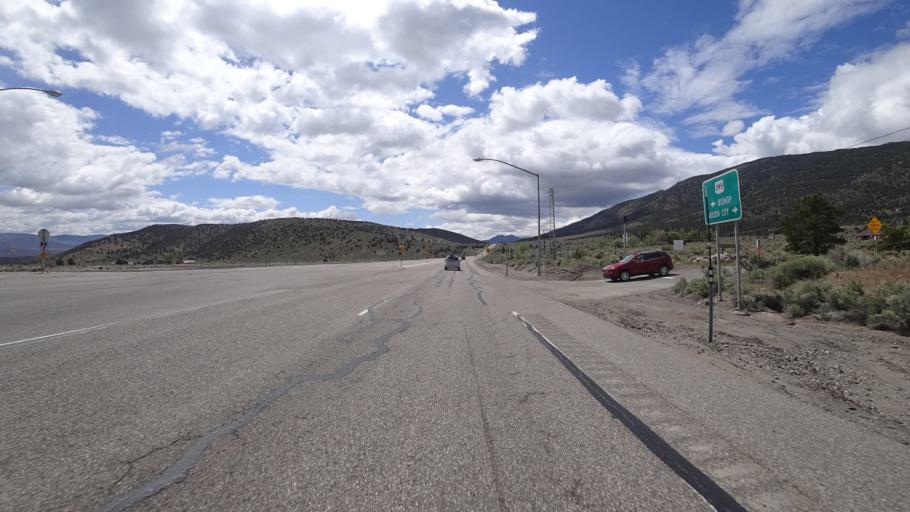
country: US
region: Nevada
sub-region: Lyon County
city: Smith Valley
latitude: 38.7284
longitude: -119.5555
